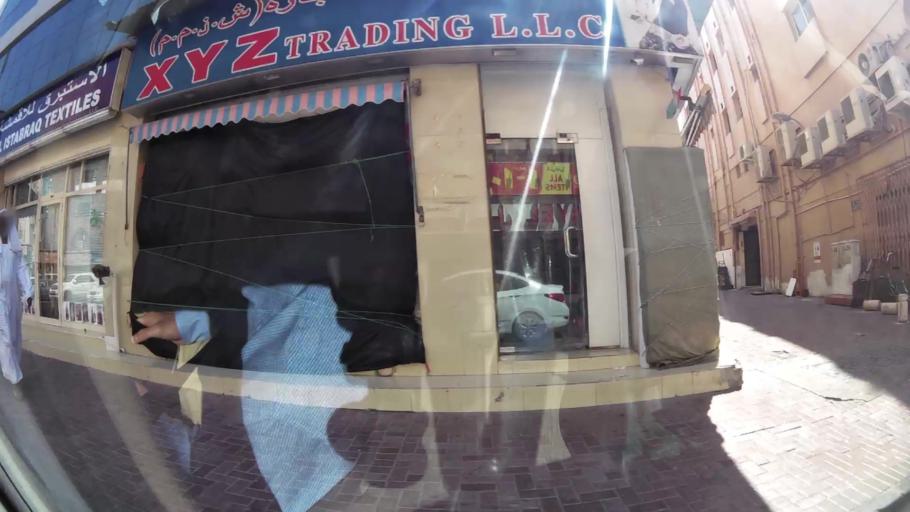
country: AE
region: Ash Shariqah
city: Sharjah
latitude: 25.2703
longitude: 55.3008
